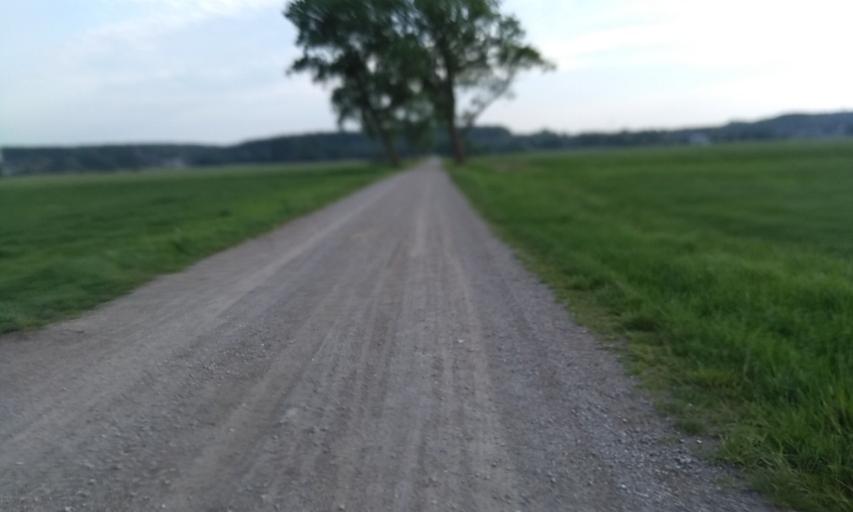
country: DE
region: Lower Saxony
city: Nottensdorf
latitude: 53.4910
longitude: 9.6358
